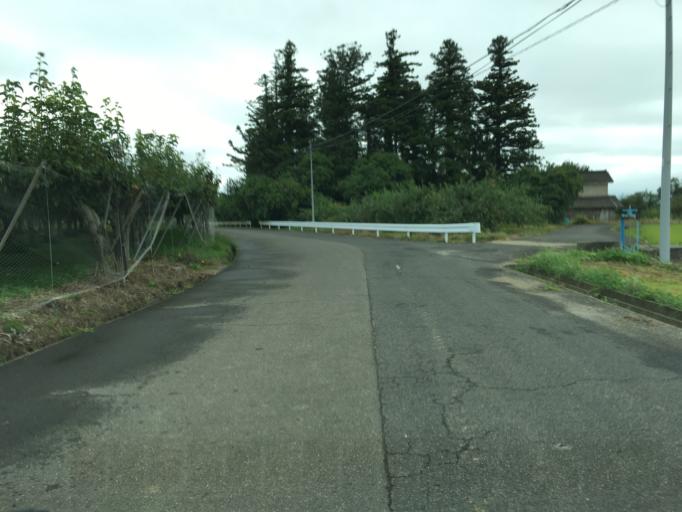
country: JP
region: Fukushima
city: Fukushima-shi
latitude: 37.7660
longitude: 140.4028
